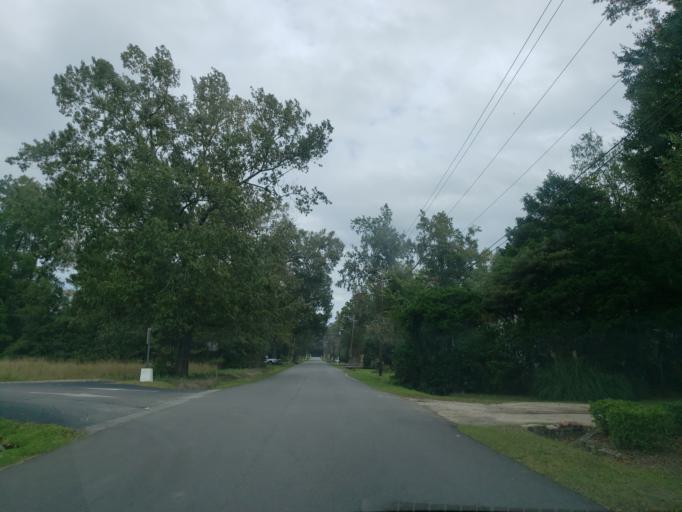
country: US
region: Georgia
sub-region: Chatham County
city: Pooler
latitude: 32.1148
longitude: -81.2438
